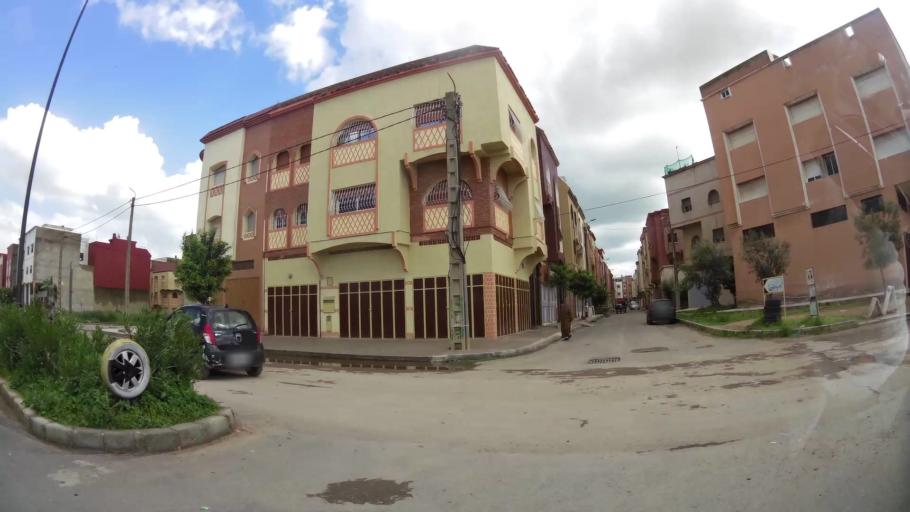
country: MA
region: Grand Casablanca
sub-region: Mediouna
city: Mediouna
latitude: 33.3785
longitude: -7.5334
